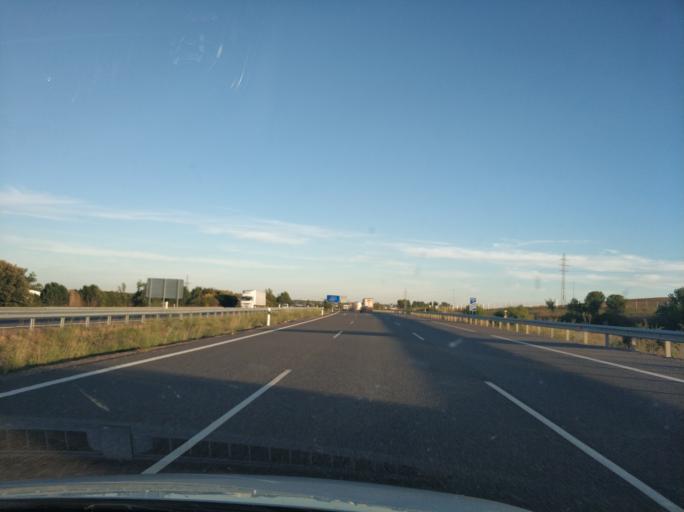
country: ES
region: Castille and Leon
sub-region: Provincia de Zamora
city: Benavente
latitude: 42.0227
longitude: -5.6700
